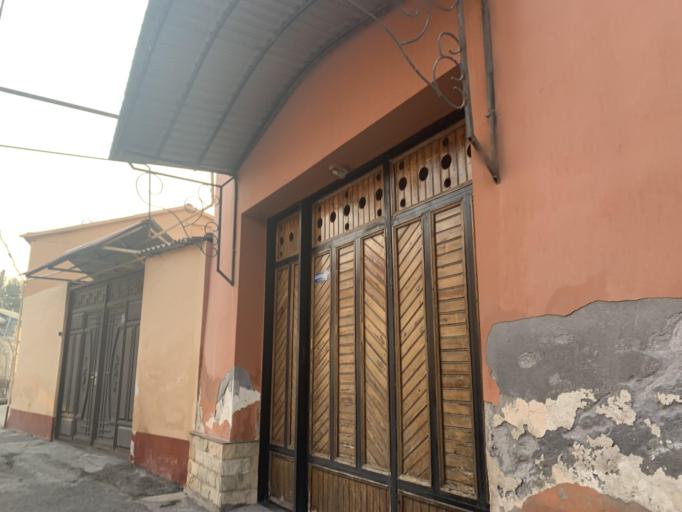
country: UZ
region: Fergana
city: Qo`qon
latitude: 40.5324
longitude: 70.9311
